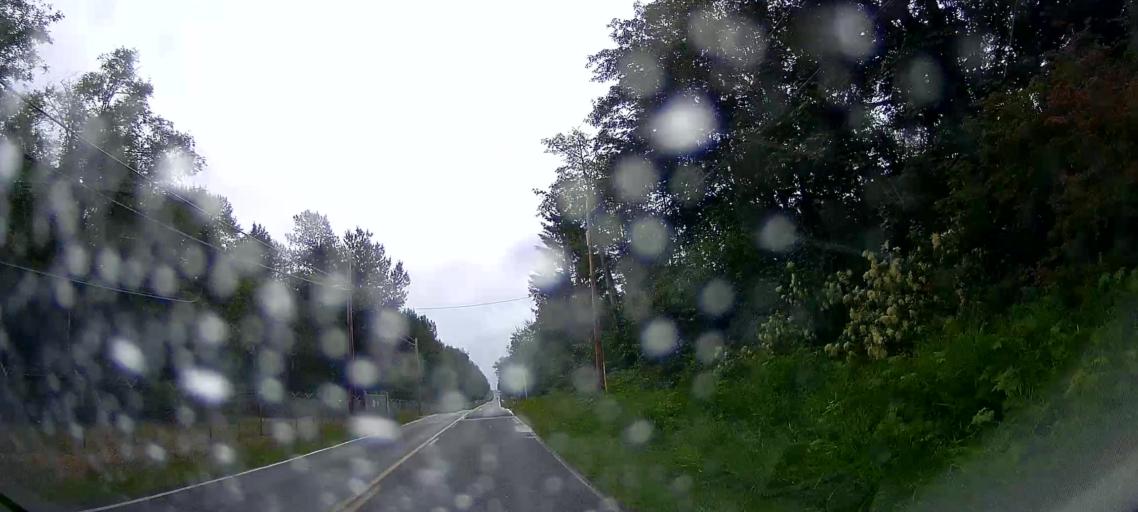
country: US
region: Washington
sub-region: Whatcom County
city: Ferndale
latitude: 48.8196
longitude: -122.6943
